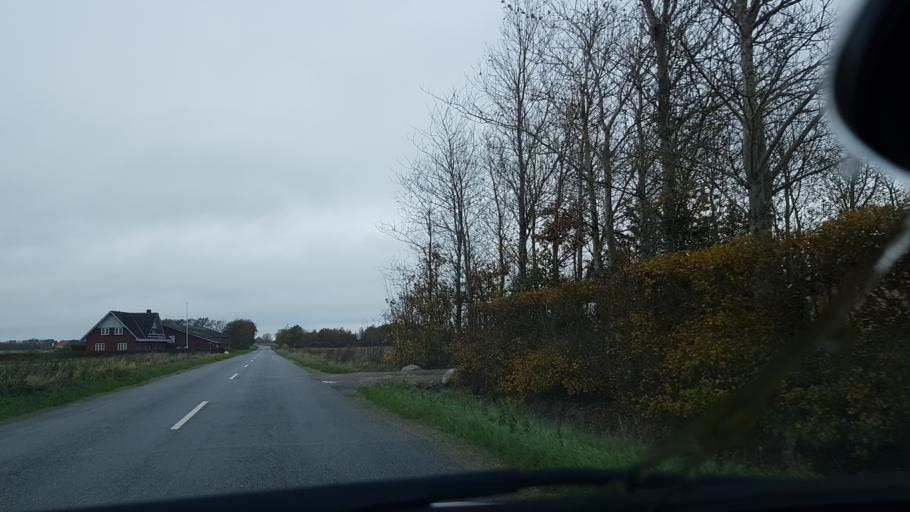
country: DK
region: South Denmark
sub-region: Tonder Kommune
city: Sherrebek
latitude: 55.2330
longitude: 8.8352
